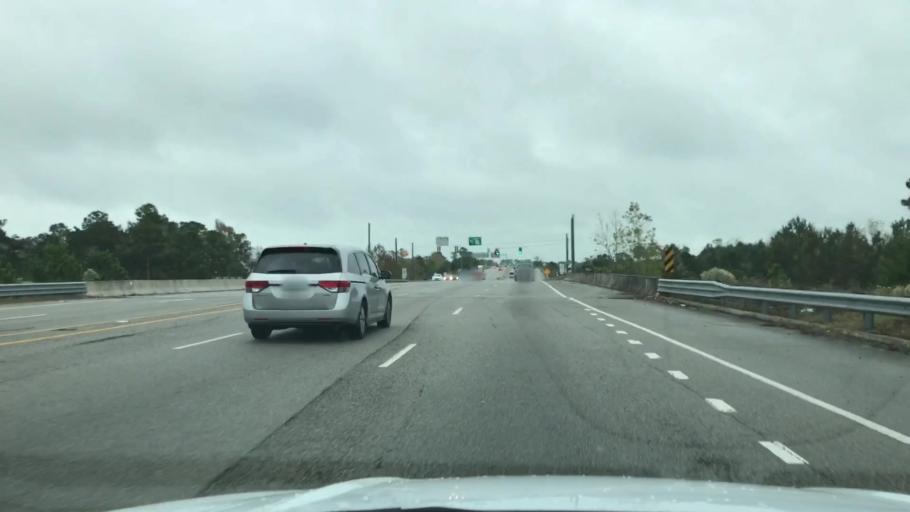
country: US
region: South Carolina
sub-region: Horry County
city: Myrtle Beach
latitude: 33.7545
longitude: -78.8530
